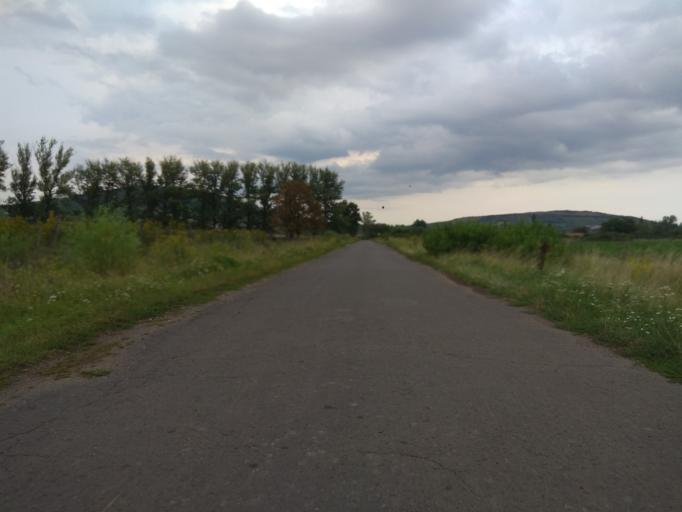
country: HU
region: Borsod-Abauj-Zemplen
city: Bekecs
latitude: 48.1579
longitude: 21.1357
